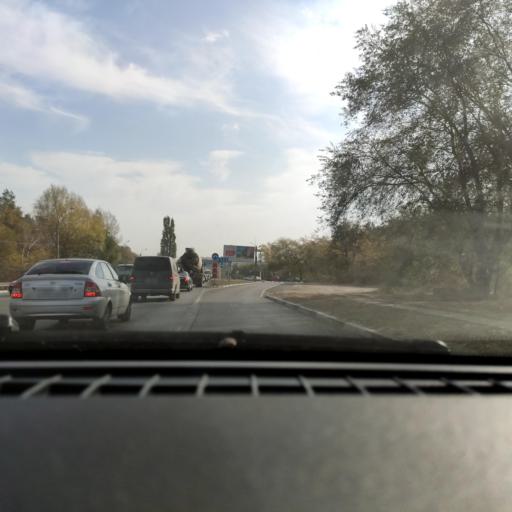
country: RU
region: Voronezj
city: Voronezh
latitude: 51.6835
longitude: 39.2759
